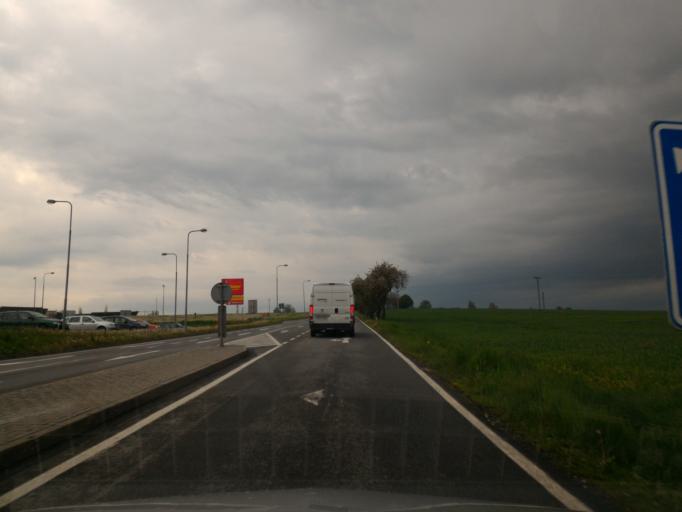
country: CZ
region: Vysocina
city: Ledec nad Sazavou
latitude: 49.6851
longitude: 15.2746
